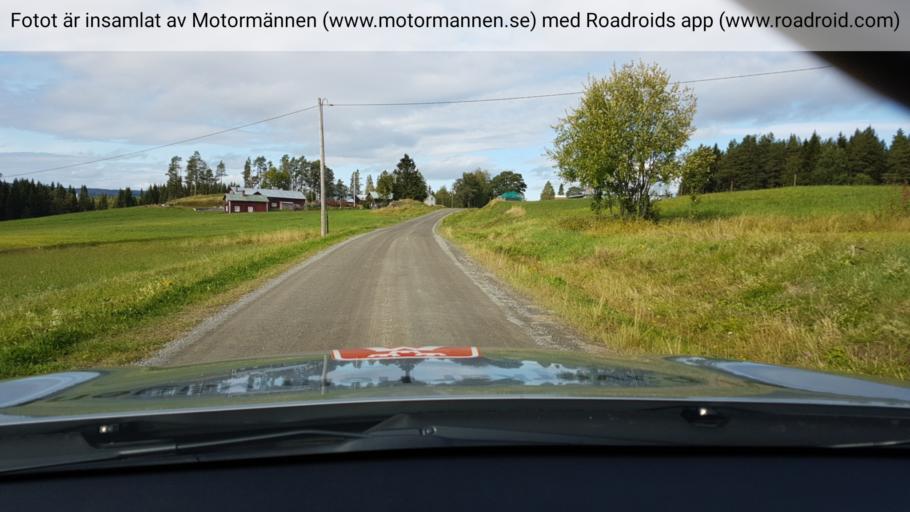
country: SE
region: Jaemtland
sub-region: Bergs Kommun
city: Hoverberg
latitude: 62.9384
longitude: 14.3989
